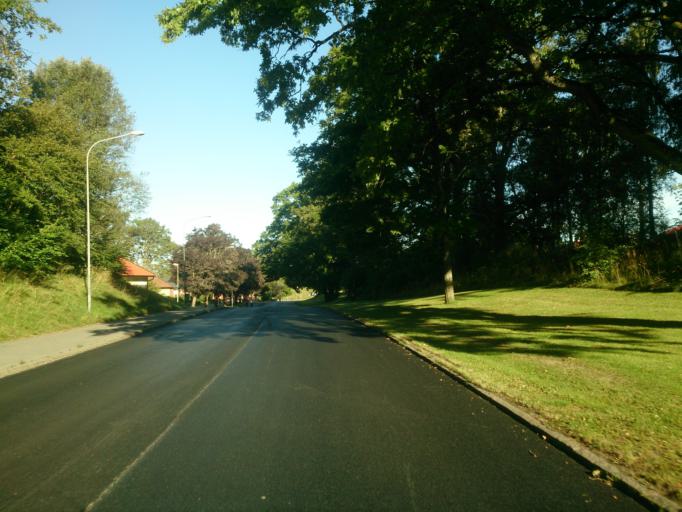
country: SE
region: OEstergoetland
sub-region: Atvidabergs Kommun
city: Atvidaberg
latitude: 58.1894
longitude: 16.0067
